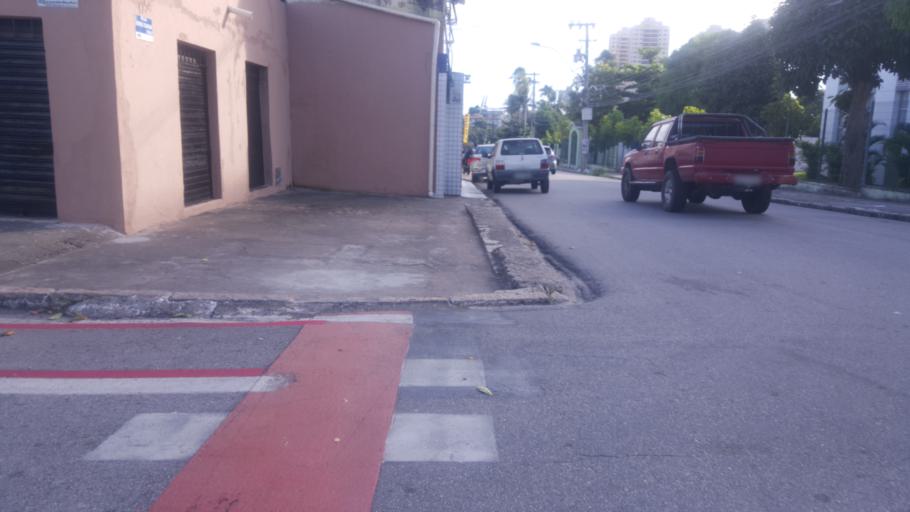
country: BR
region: Ceara
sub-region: Fortaleza
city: Fortaleza
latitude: -3.7520
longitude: -38.5393
